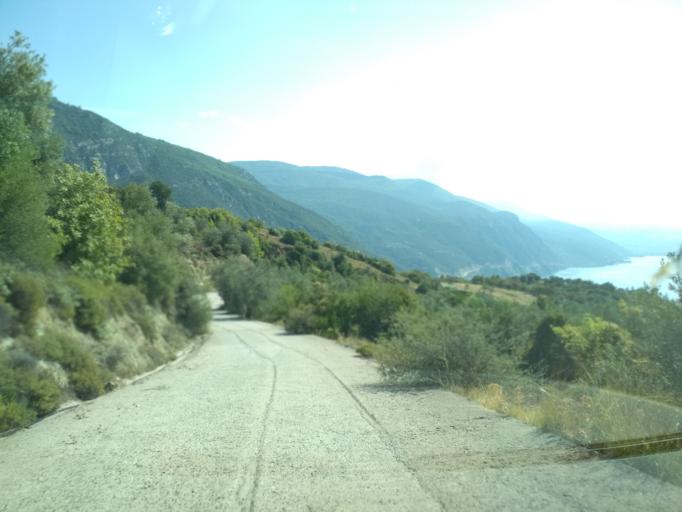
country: GR
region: Central Greece
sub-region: Nomos Evvoias
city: Oreoi
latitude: 38.8520
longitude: 23.1072
